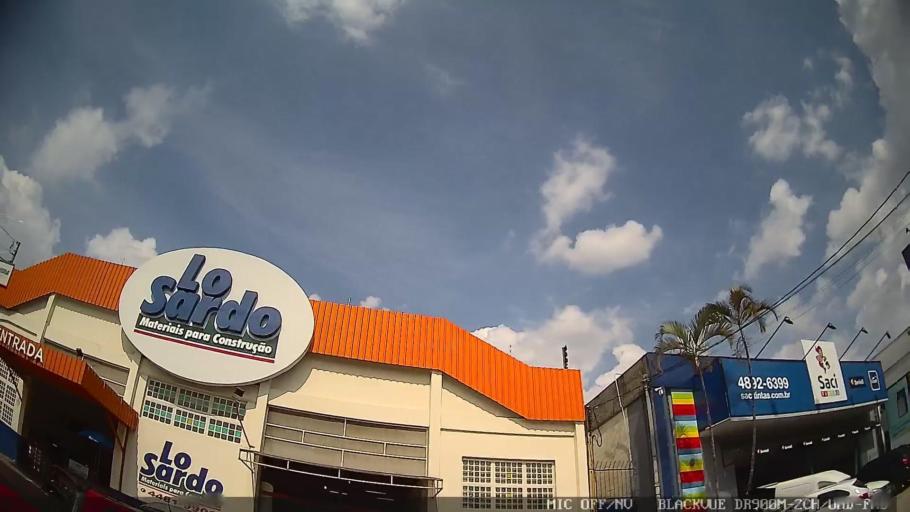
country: BR
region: Sao Paulo
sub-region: Braganca Paulista
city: Braganca Paulista
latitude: -22.9618
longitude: -46.5428
